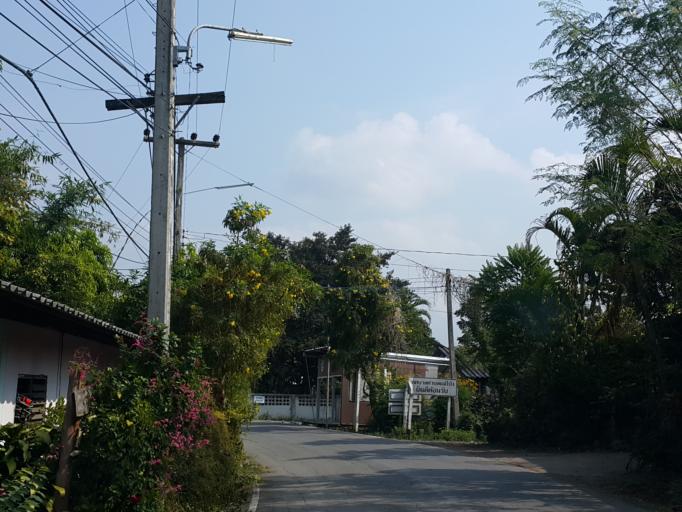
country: TH
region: Chiang Mai
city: San Kamphaeng
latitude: 18.8164
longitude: 99.1606
